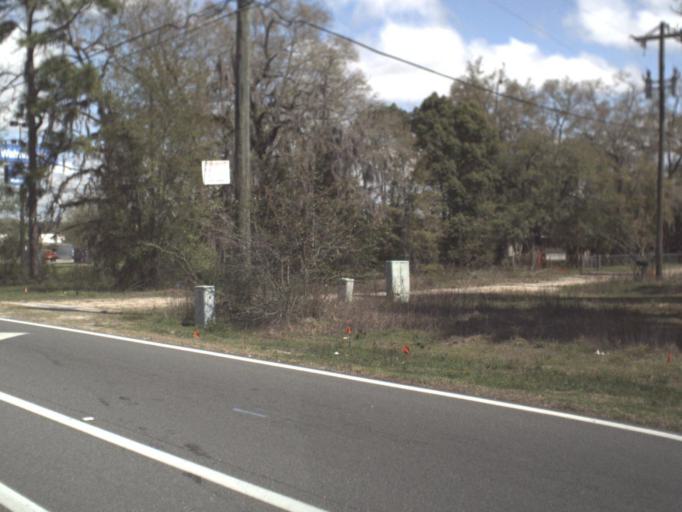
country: US
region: Florida
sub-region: Wakulla County
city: Crawfordville
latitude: 30.2151
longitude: -84.3630
